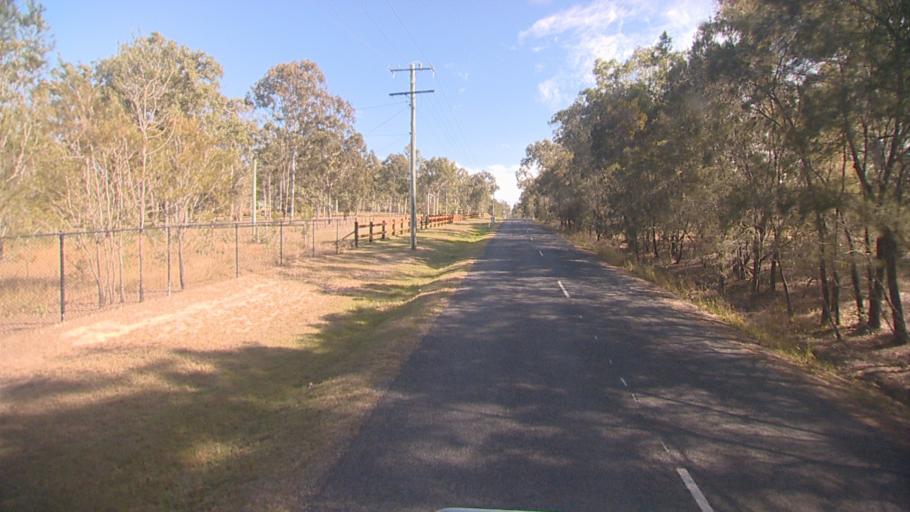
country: AU
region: Queensland
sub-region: Logan
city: North Maclean
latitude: -27.7666
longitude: 152.9795
